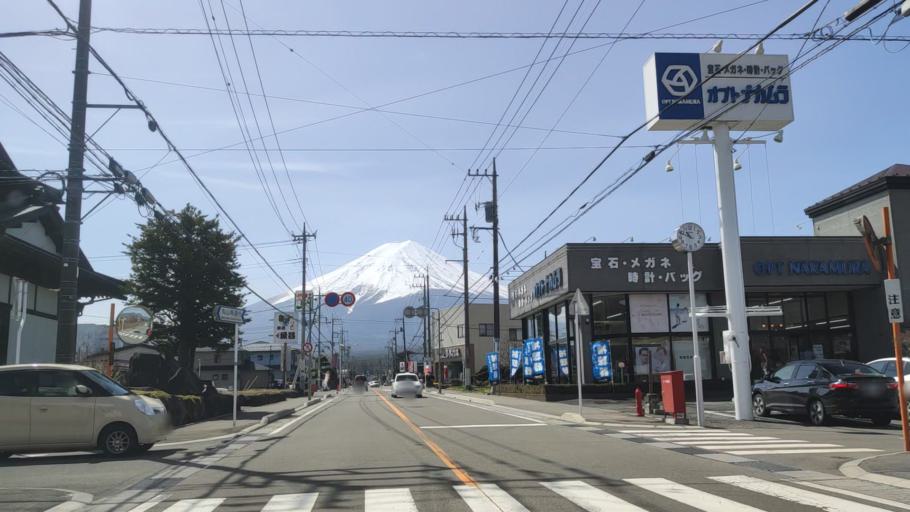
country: JP
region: Yamanashi
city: Fujikawaguchiko
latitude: 35.4924
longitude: 138.7636
